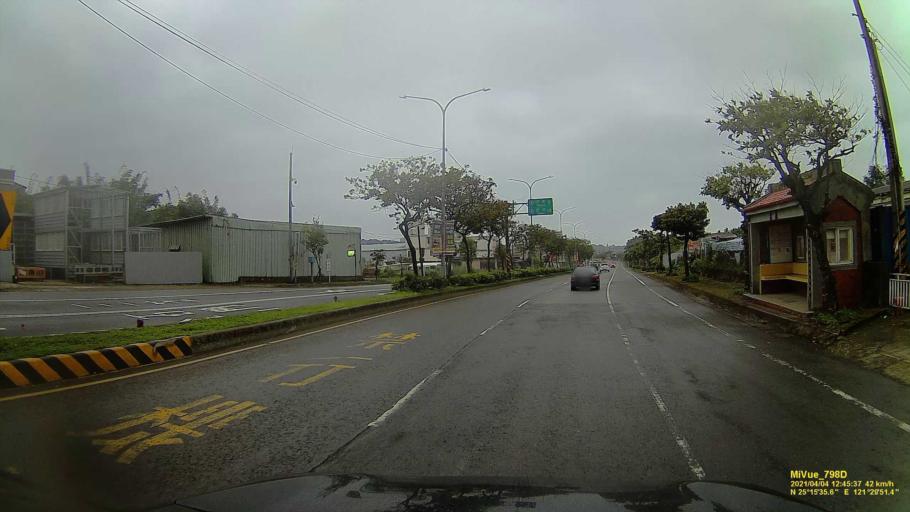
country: TW
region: Taipei
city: Taipei
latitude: 25.2599
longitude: 121.4973
